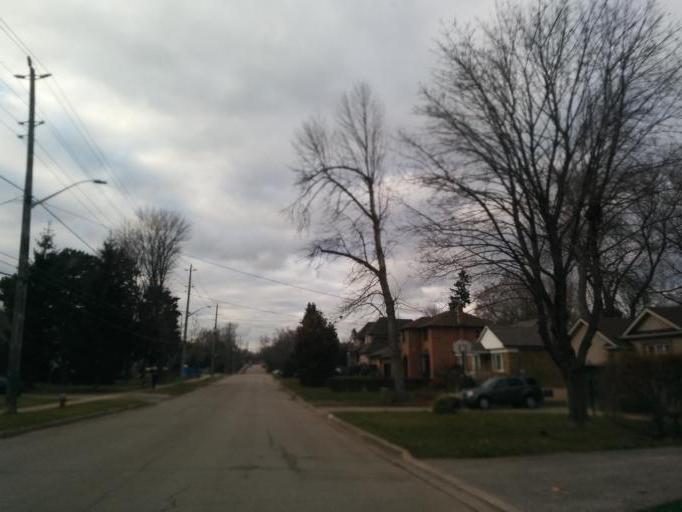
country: CA
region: Ontario
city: Etobicoke
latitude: 43.5891
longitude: -79.5682
